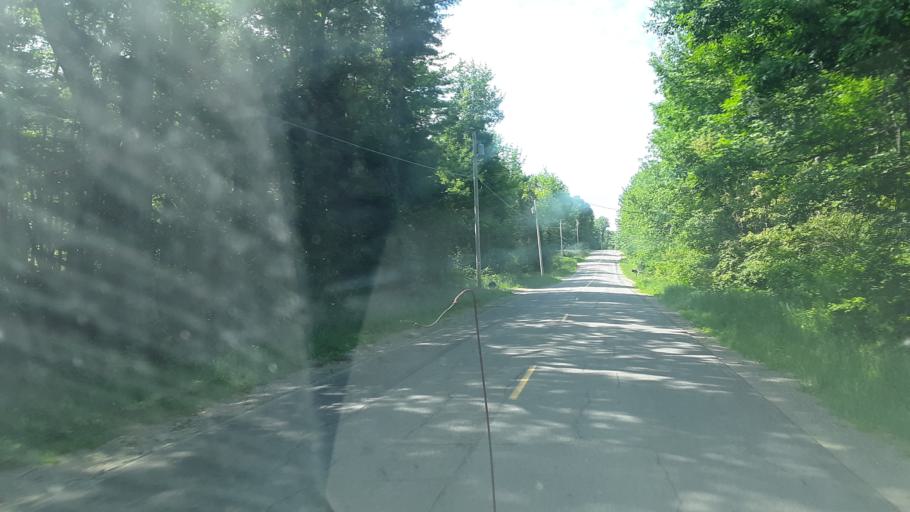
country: US
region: Maine
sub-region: Waldo County
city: Swanville
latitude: 44.5763
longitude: -68.9490
